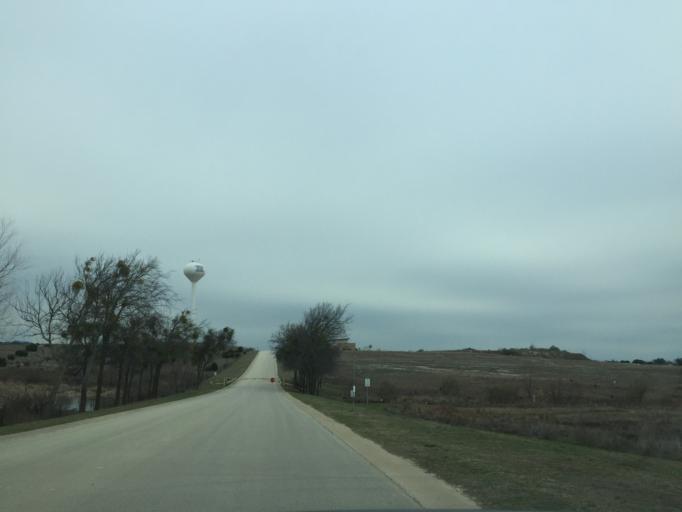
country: US
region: Texas
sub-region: Bell County
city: Fort Hood
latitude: 31.1141
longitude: -97.8099
